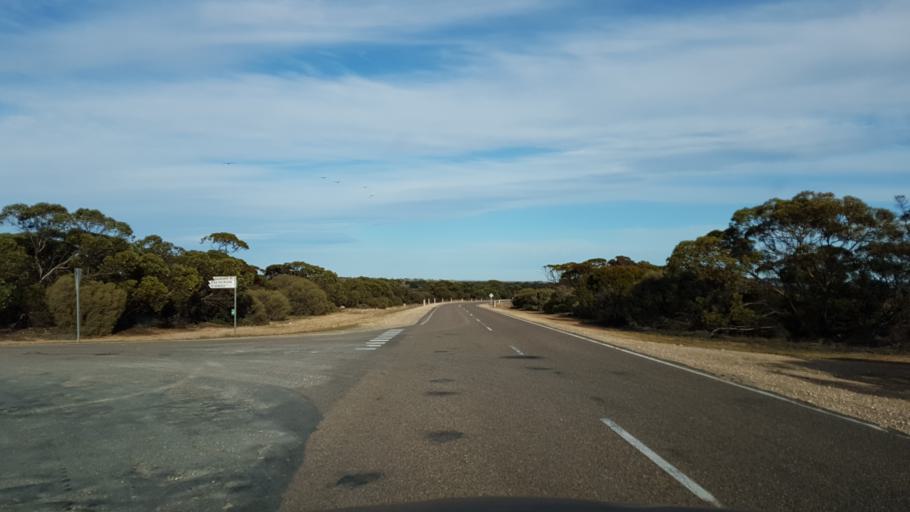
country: AU
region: South Australia
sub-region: Mid Murray
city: Mannum
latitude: -35.0428
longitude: 139.4648
